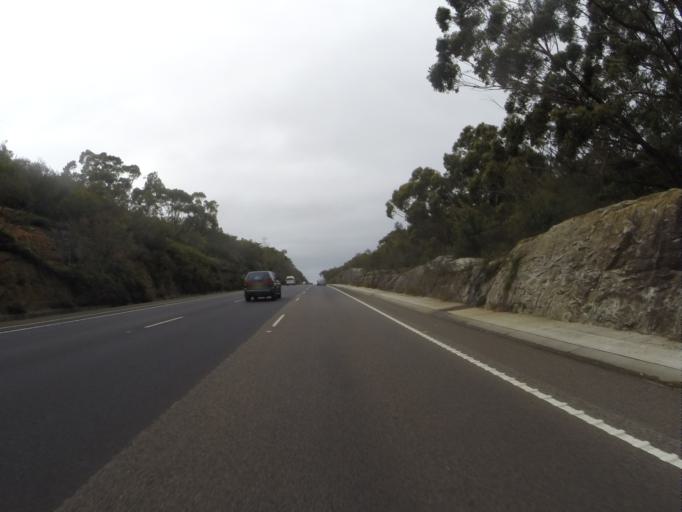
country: AU
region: New South Wales
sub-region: Wollongong
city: Bulli
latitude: -34.2998
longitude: 150.9104
